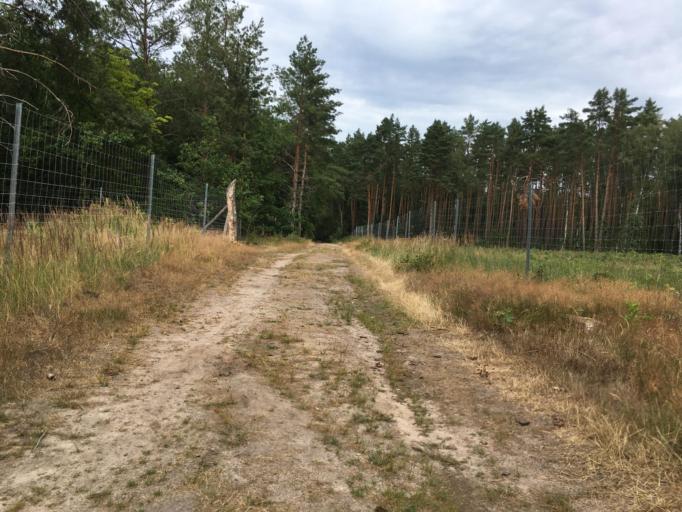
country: DE
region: Brandenburg
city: Wandlitz
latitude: 52.7357
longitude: 13.5057
